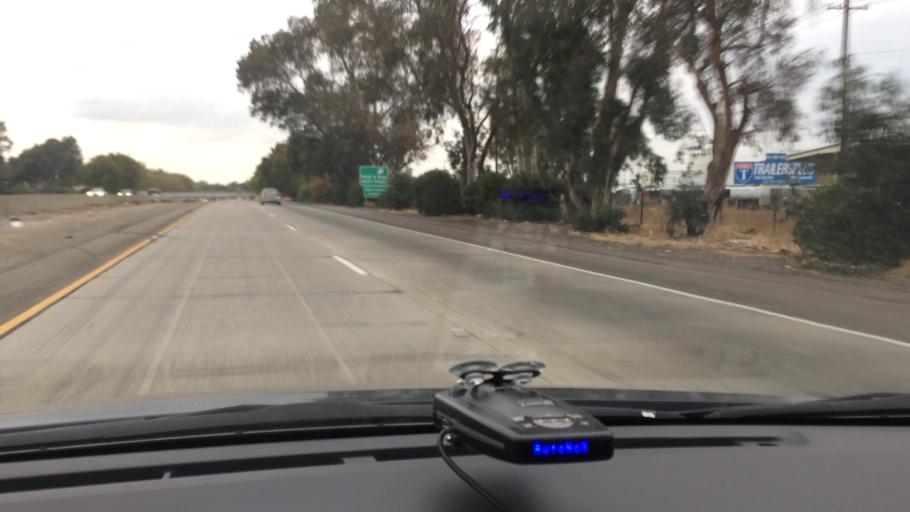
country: US
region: California
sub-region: San Joaquin County
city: Lodi
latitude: 38.1268
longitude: -121.2573
